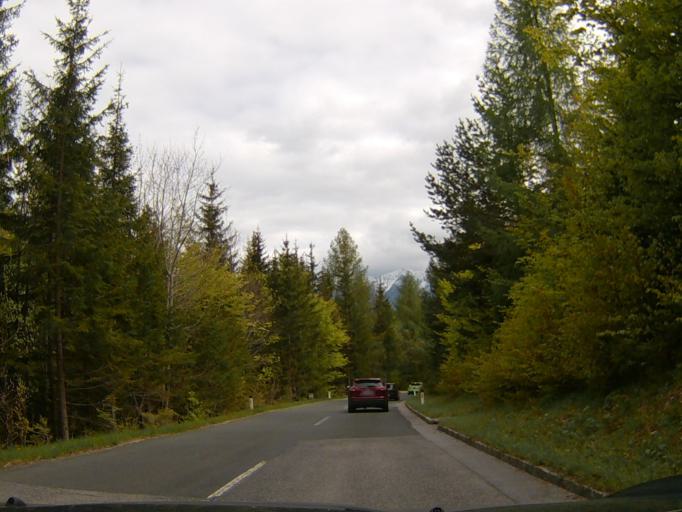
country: AT
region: Carinthia
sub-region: Politischer Bezirk Villach Land
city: Arnoldstein
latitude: 46.5878
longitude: 13.7771
